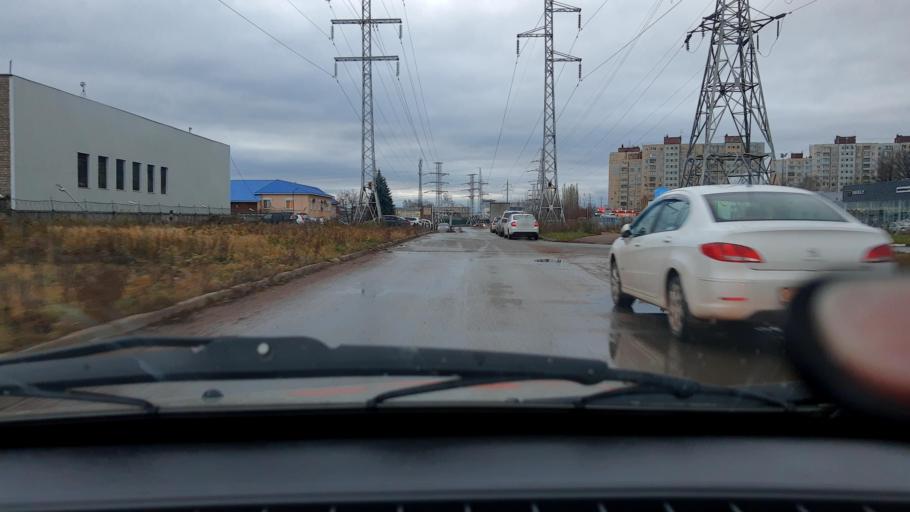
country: RU
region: Bashkortostan
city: Ufa
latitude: 54.7996
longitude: 56.0566
